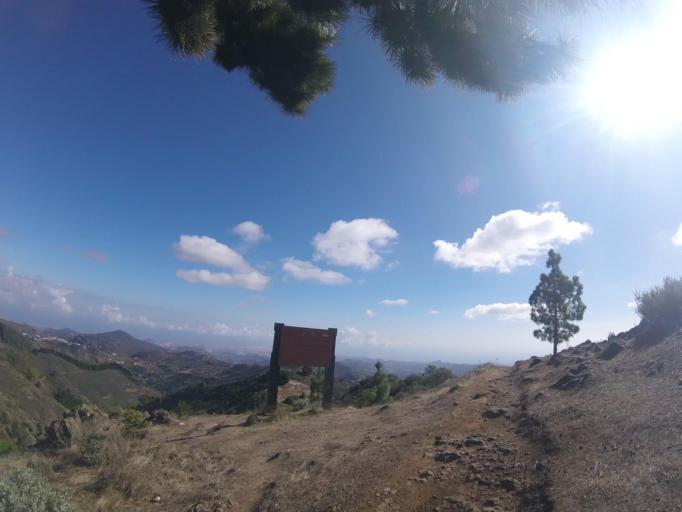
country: ES
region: Canary Islands
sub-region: Provincia de Las Palmas
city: Valleseco
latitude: 28.0173
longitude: -15.5819
